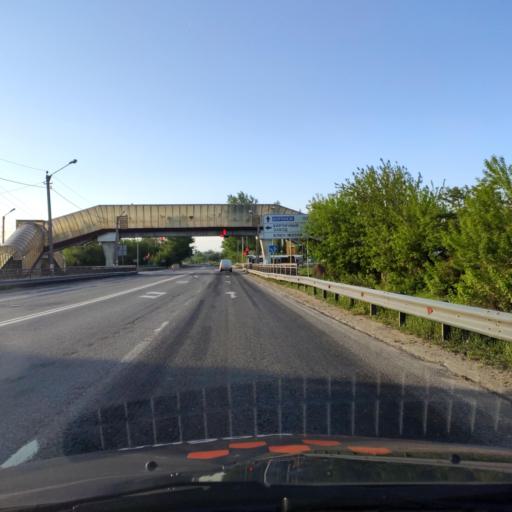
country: RU
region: Lipetsk
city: Yelets
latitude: 52.6006
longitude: 38.4724
